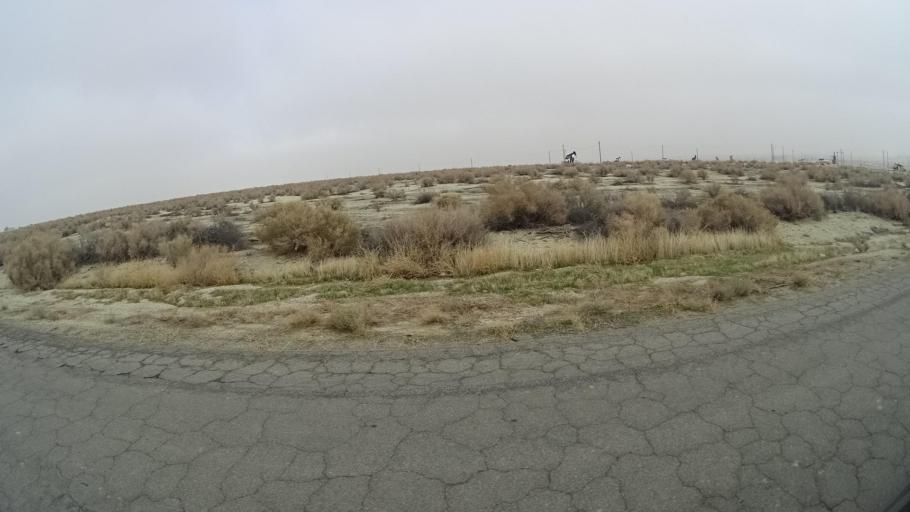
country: US
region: California
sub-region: Kern County
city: Maricopa
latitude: 35.0454
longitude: -119.3891
